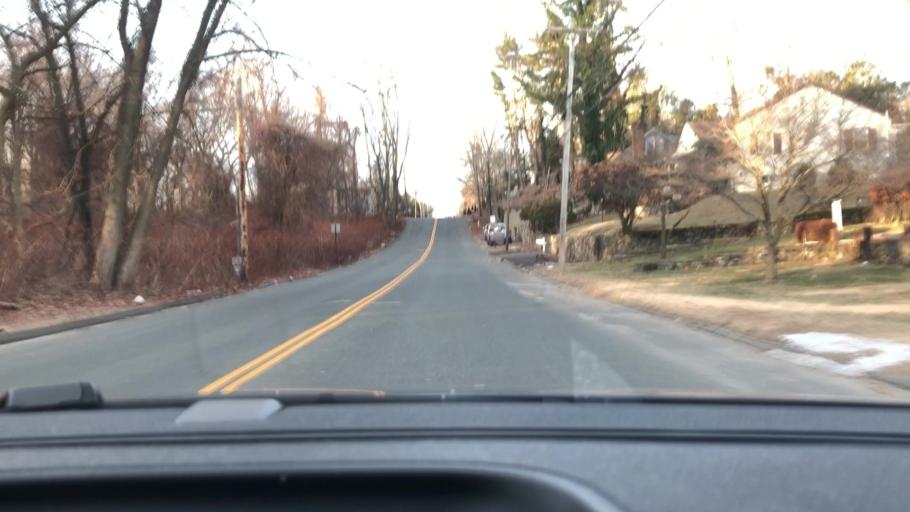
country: US
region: Connecticut
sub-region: Fairfield County
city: Trumbull
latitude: 41.2283
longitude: -73.2130
